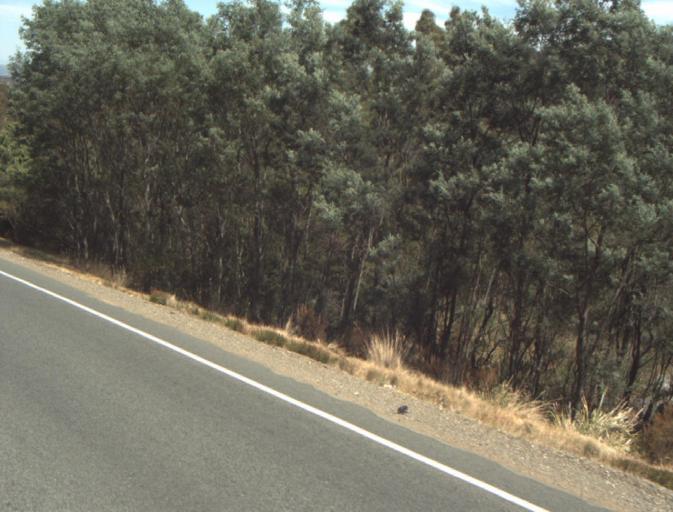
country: AU
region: Tasmania
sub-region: Launceston
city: Mayfield
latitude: -41.3509
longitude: 147.1431
